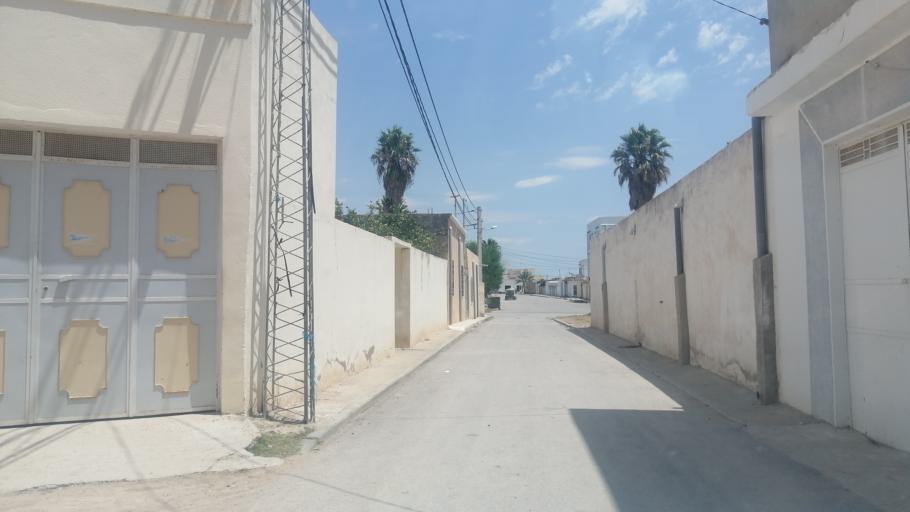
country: TN
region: Al Qayrawan
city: Sbikha
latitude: 36.1215
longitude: 10.0921
